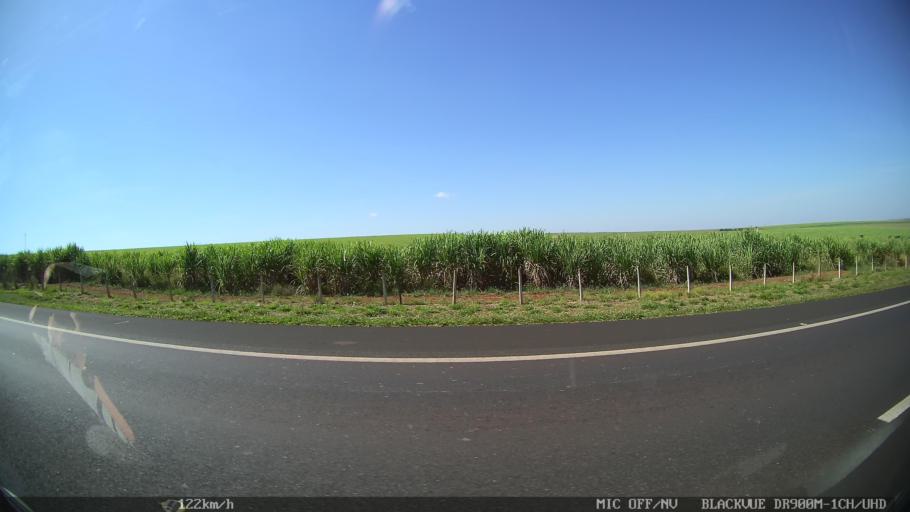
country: BR
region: Sao Paulo
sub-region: Franca
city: Franca
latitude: -20.6839
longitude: -47.4964
